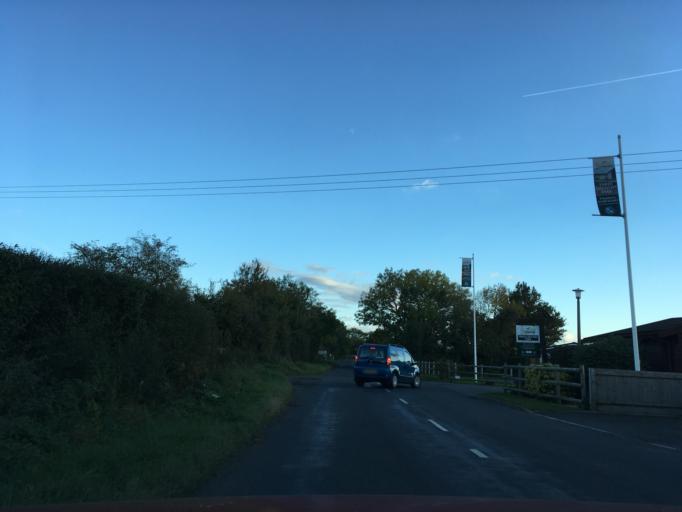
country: GB
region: England
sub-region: Worcestershire
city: Upton upon Severn
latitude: 52.0101
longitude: -2.2797
